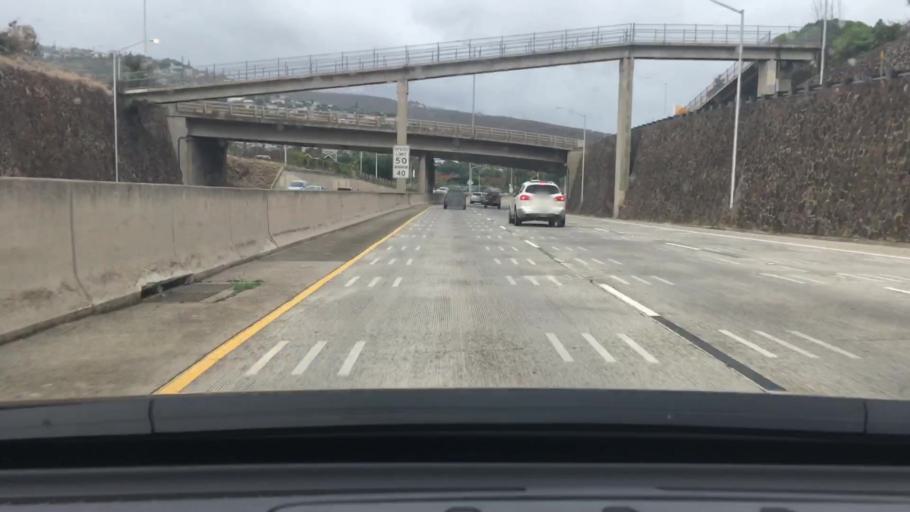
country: US
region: Hawaii
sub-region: Honolulu County
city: Honolulu
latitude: 21.2788
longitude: -157.7929
